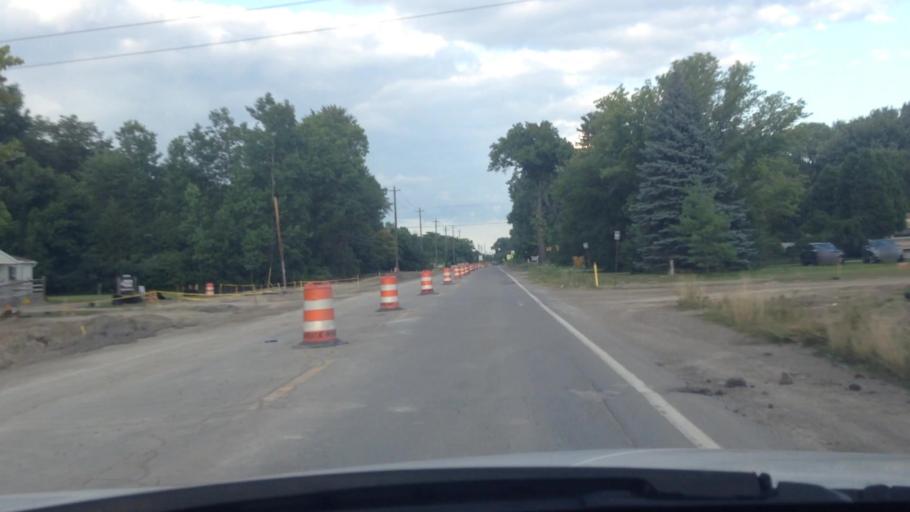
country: US
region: Michigan
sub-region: Wayne County
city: Woodhaven
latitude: 42.1681
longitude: -83.2574
